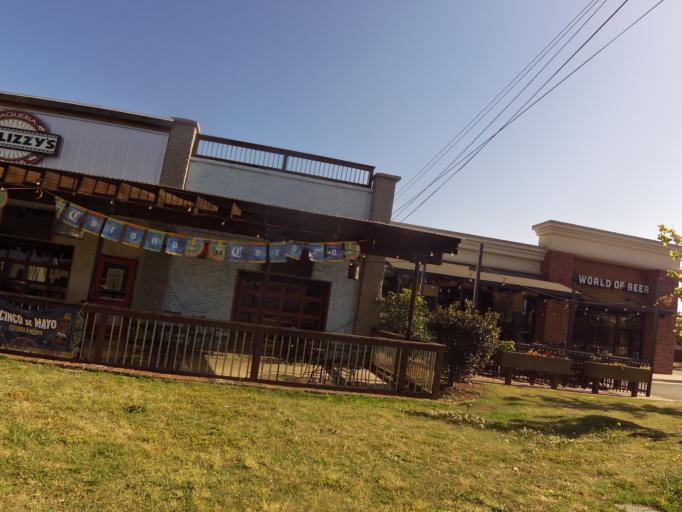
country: US
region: Georgia
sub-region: Columbia County
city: Martinez
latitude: 33.5106
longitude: -82.0315
